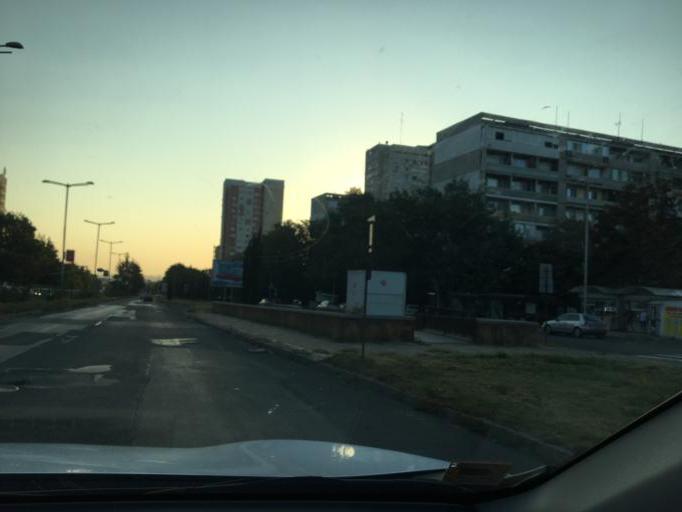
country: BG
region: Burgas
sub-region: Obshtina Burgas
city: Burgas
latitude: 42.5251
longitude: 27.4485
